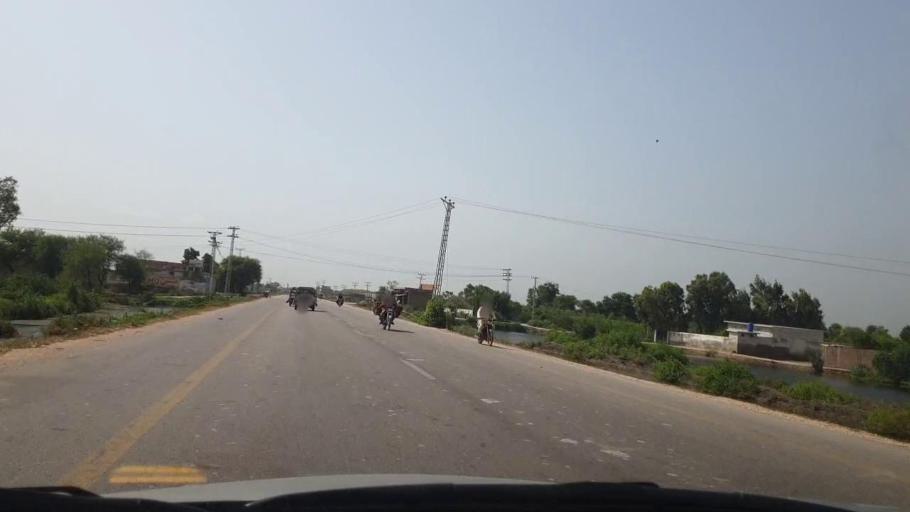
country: PK
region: Sindh
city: Matli
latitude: 25.0273
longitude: 68.6531
